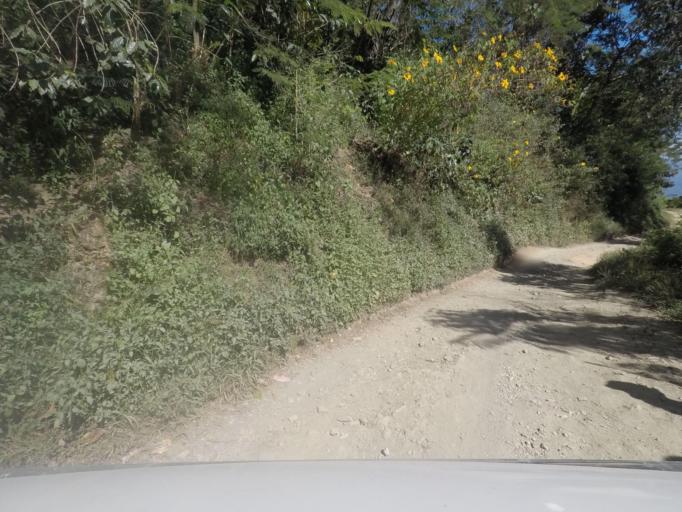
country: TL
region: Ermera
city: Gleno
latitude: -8.7238
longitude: 125.3288
